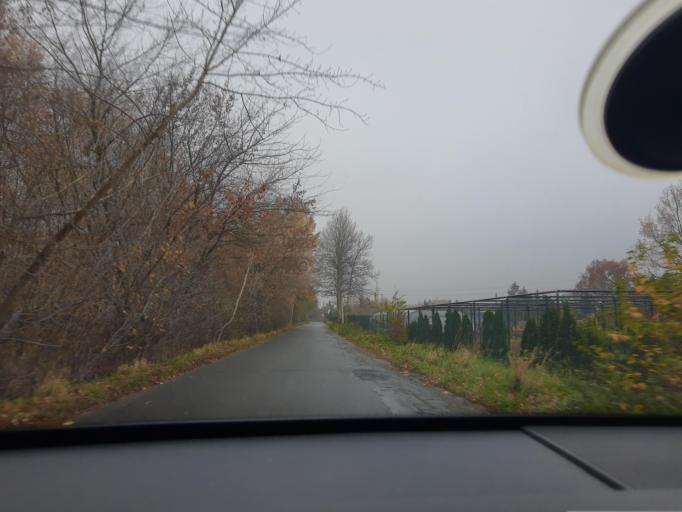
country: PL
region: Lodz Voivodeship
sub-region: Powiat pabianicki
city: Konstantynow Lodzki
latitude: 51.7495
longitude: 19.3722
